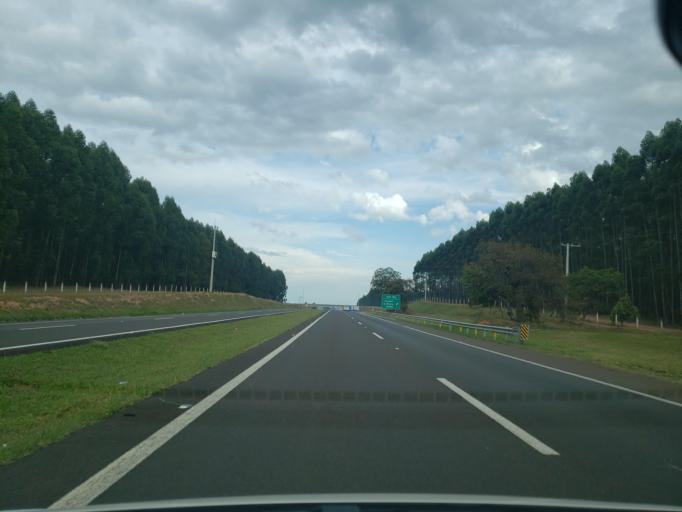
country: BR
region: Sao Paulo
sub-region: Itirapina
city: Itirapina
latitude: -22.2617
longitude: -47.8892
